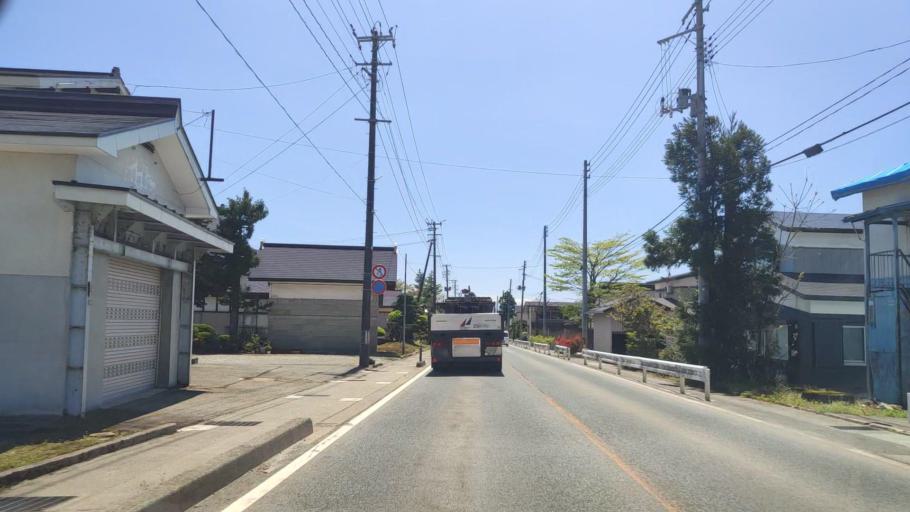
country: JP
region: Yamagata
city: Shinjo
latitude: 38.8031
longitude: 140.3206
